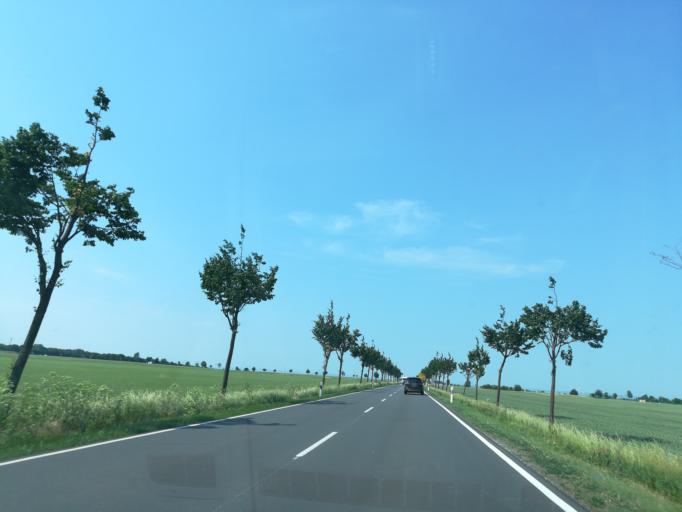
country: DE
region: Saxony-Anhalt
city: Gross Bornecke
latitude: 51.8563
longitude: 11.4501
